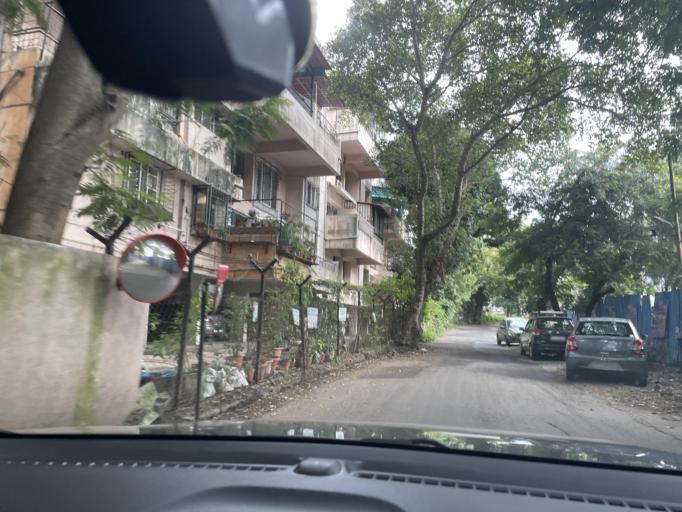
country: IN
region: Maharashtra
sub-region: Pune Division
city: Kharakvasla
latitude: 18.5125
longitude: 73.7803
